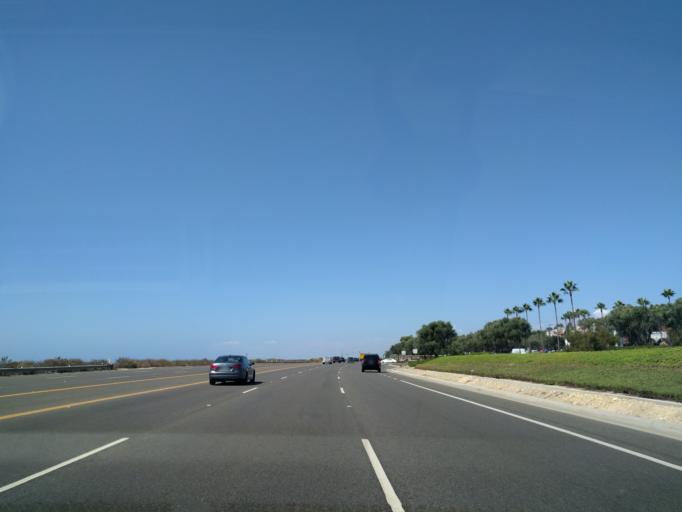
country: US
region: California
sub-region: Orange County
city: San Joaquin Hills
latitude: 33.5682
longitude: -117.8322
